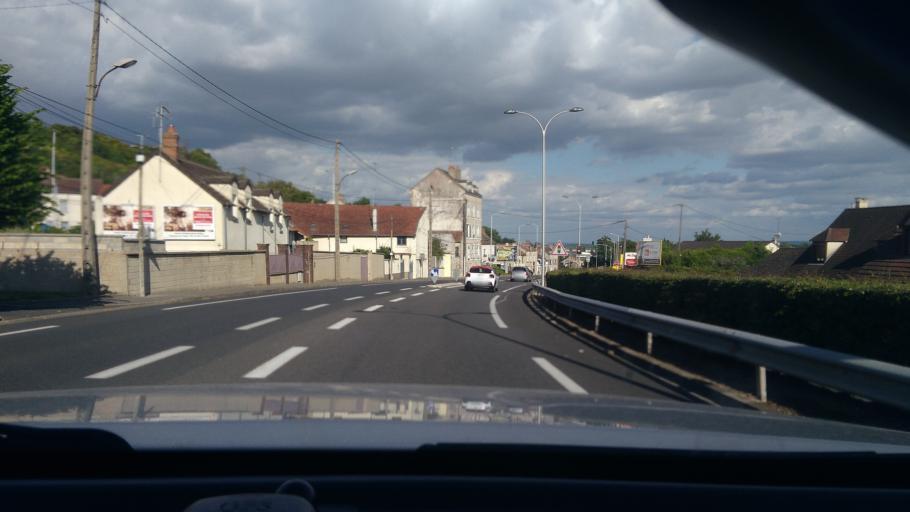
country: FR
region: Ile-de-France
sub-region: Departement de Seine-et-Marne
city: Montereau-Fault-Yonne
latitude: 48.3909
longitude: 2.9532
